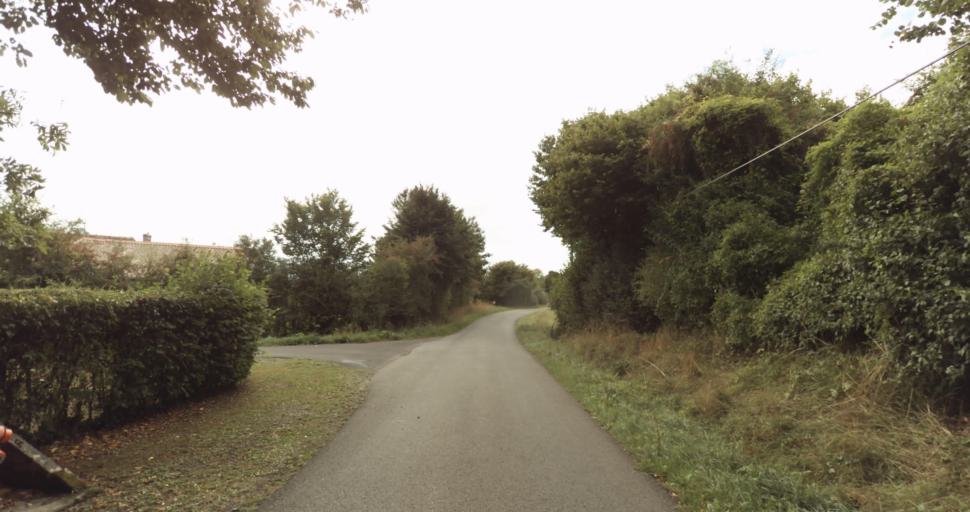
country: FR
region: Lower Normandy
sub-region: Departement de l'Orne
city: Gace
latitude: 48.7757
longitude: 0.3502
